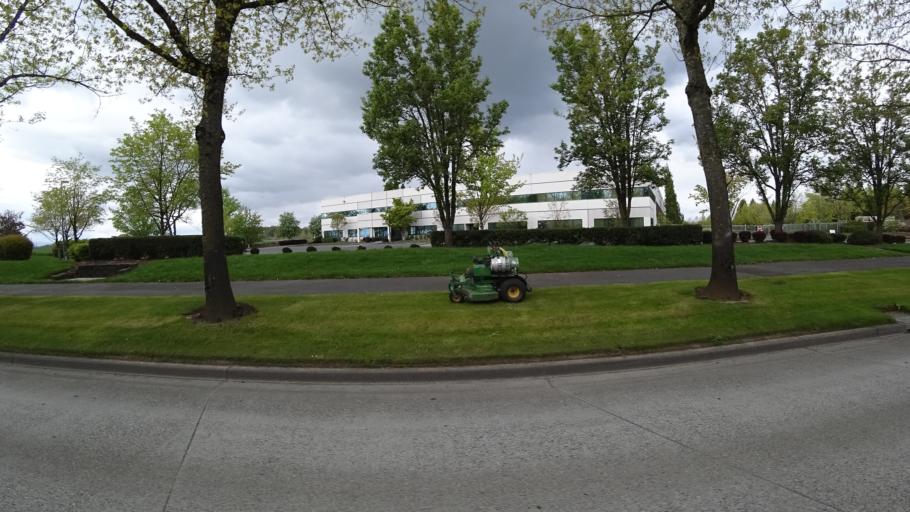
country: US
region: Oregon
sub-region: Washington County
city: Rockcreek
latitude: 45.5456
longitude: -122.9349
